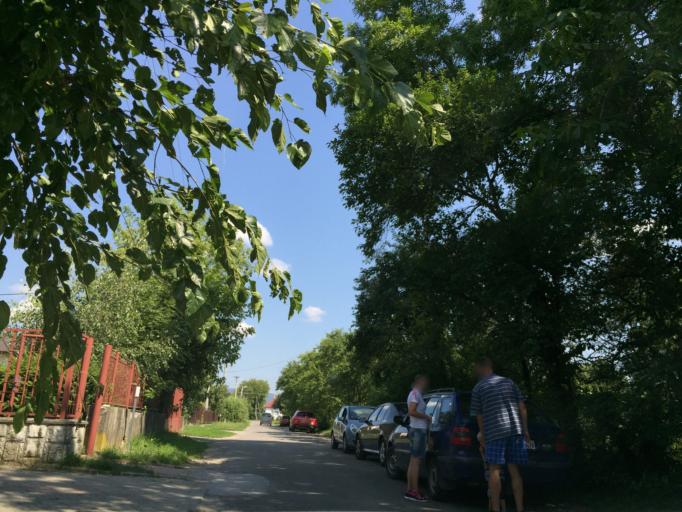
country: SK
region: Kosicky
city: Sobrance
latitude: 48.7417
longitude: 22.1819
